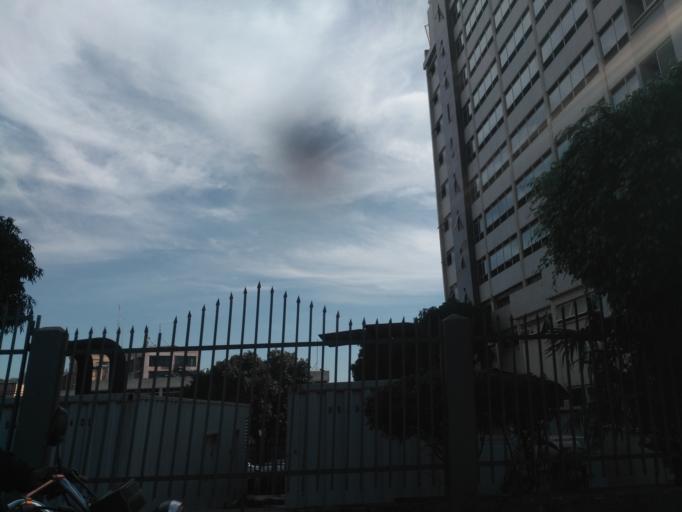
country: UG
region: Central Region
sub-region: Kampala District
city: Kampala
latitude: 0.3194
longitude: 32.5878
